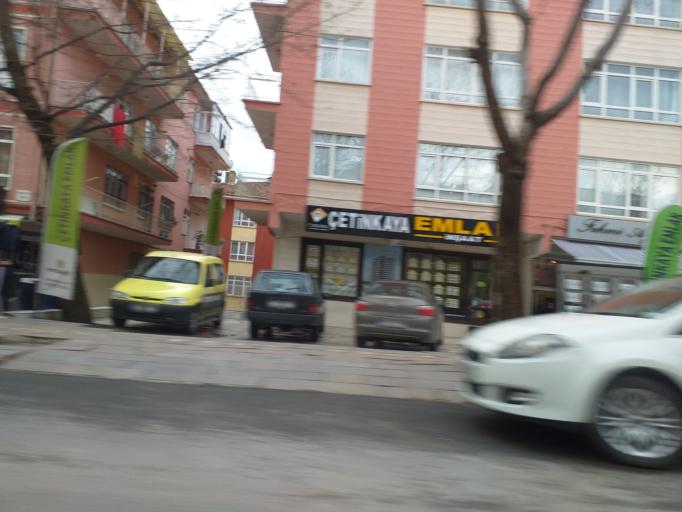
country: TR
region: Ankara
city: Ankara
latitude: 39.9727
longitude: 32.8317
